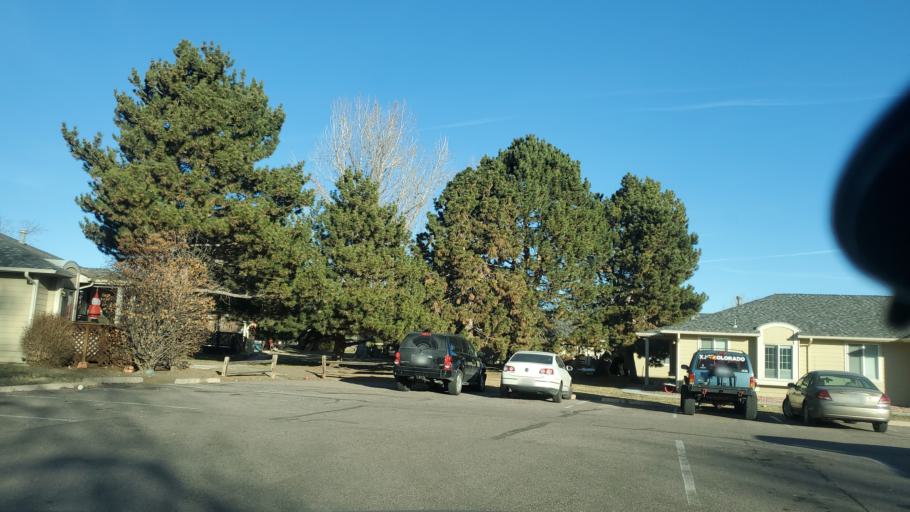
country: US
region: Colorado
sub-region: Adams County
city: Welby
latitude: 39.8396
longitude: -104.9609
